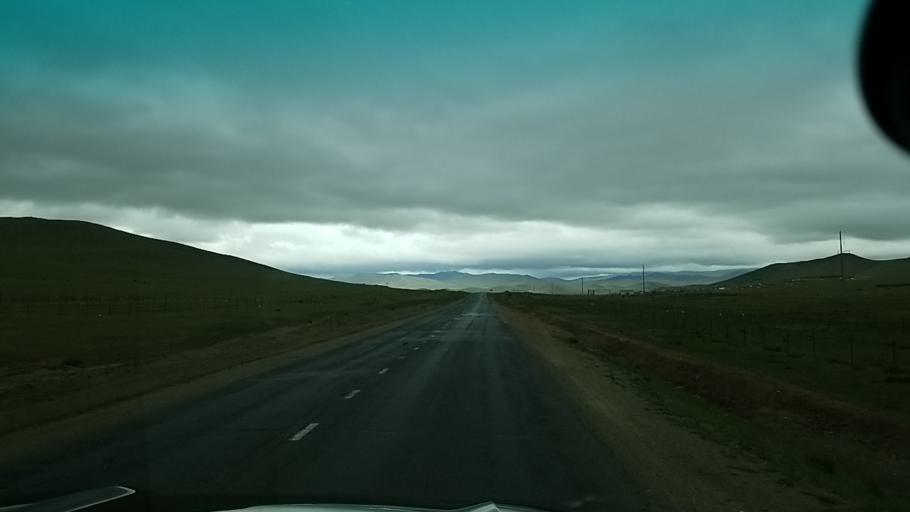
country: MN
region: Ulaanbaatar
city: Ulaanbaatar
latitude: 47.9835
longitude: 106.5672
